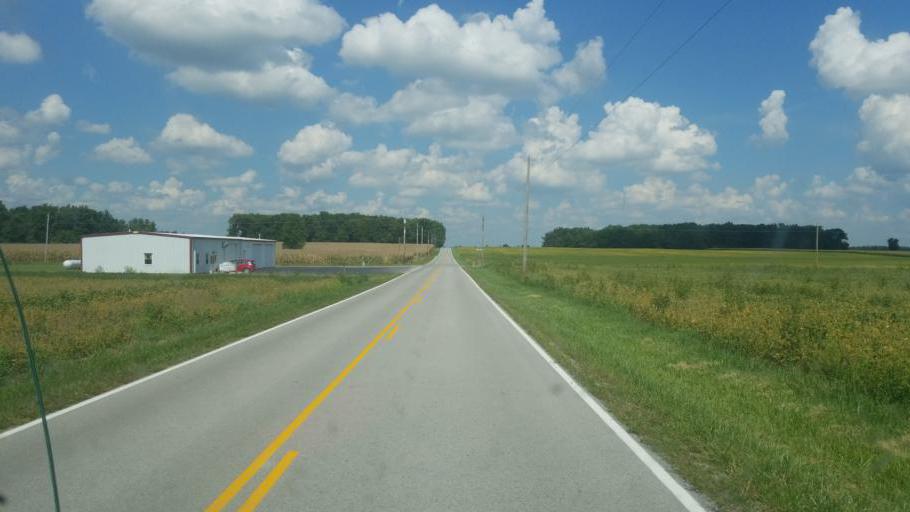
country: US
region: Ohio
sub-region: Hancock County
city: Arlington
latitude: 40.8620
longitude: -83.7274
